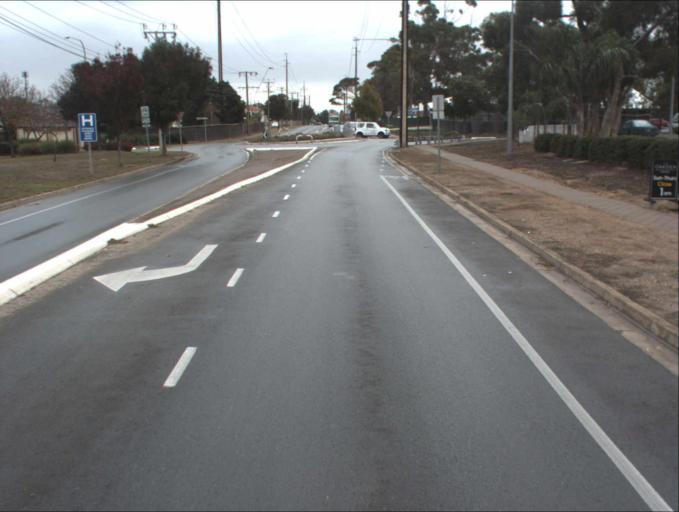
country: AU
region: South Australia
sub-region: Port Adelaide Enfield
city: Gilles Plains
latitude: -34.8520
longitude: 138.6357
